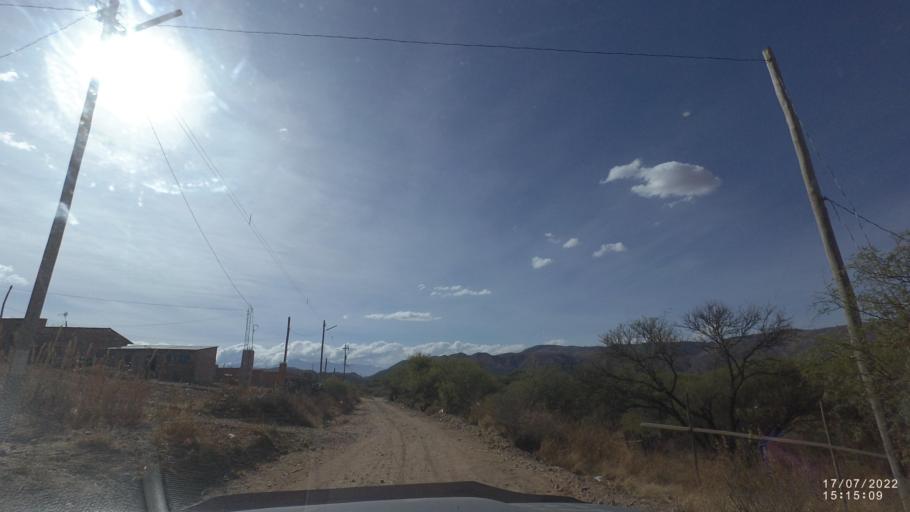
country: BO
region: Cochabamba
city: Capinota
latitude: -17.5585
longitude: -66.2619
